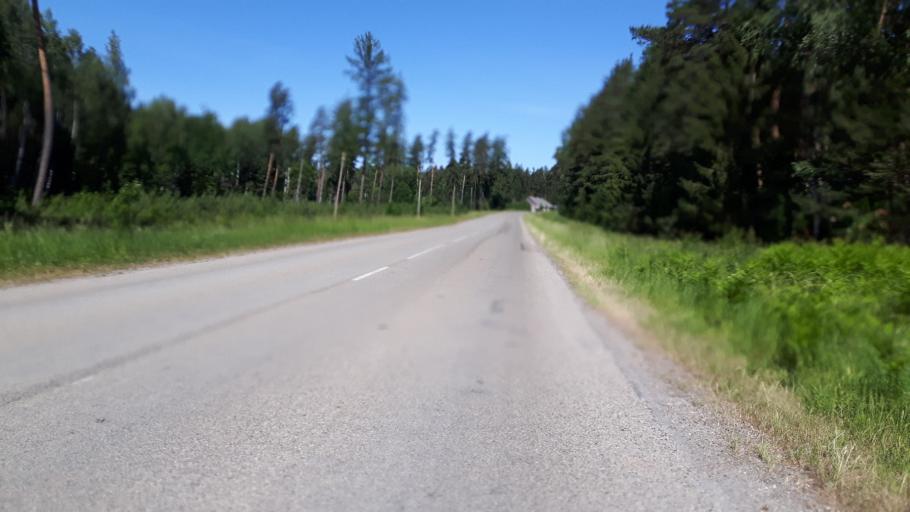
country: LV
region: Tukuma Rajons
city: Tukums
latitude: 57.0098
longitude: 23.0552
